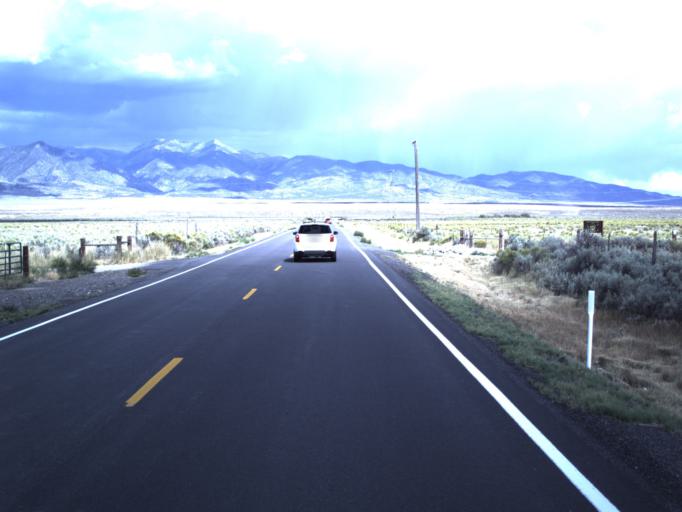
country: US
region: Utah
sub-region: Tooele County
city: Tooele
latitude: 40.3369
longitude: -112.4235
